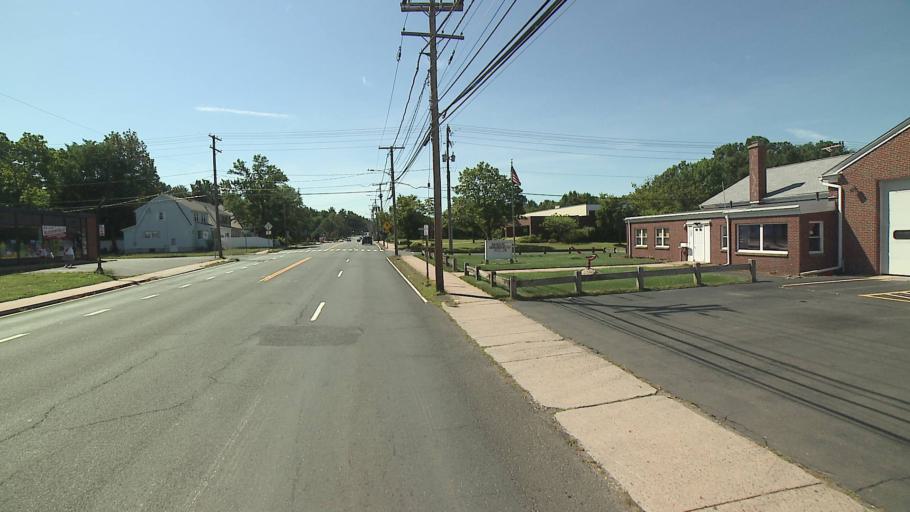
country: US
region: Connecticut
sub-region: Hartford County
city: Blue Hills
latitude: 41.8202
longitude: -72.6959
